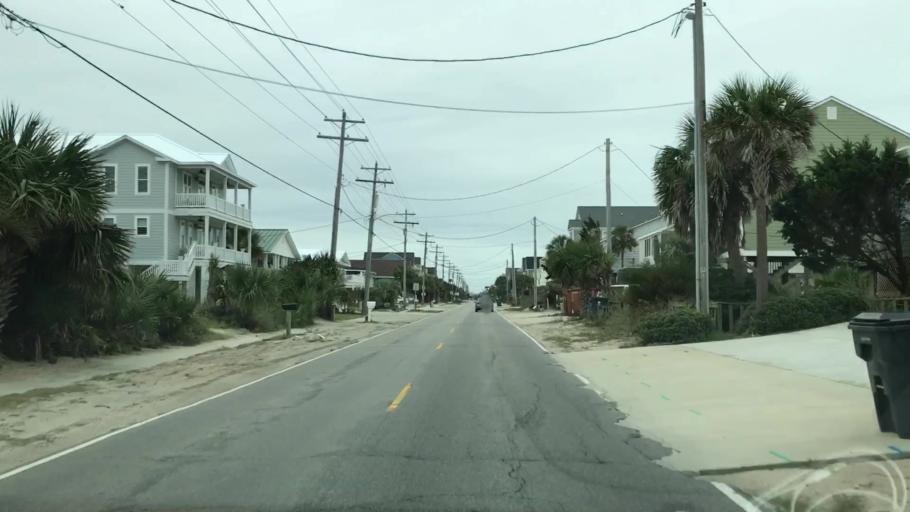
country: US
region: South Carolina
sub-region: Horry County
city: Garden City
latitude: 33.5703
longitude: -79.0044
